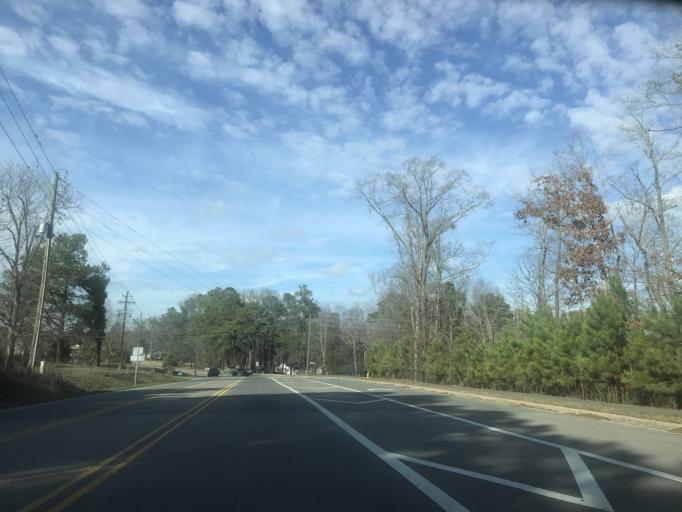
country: US
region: North Carolina
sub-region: Wake County
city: Garner
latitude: 35.7249
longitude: -78.5493
